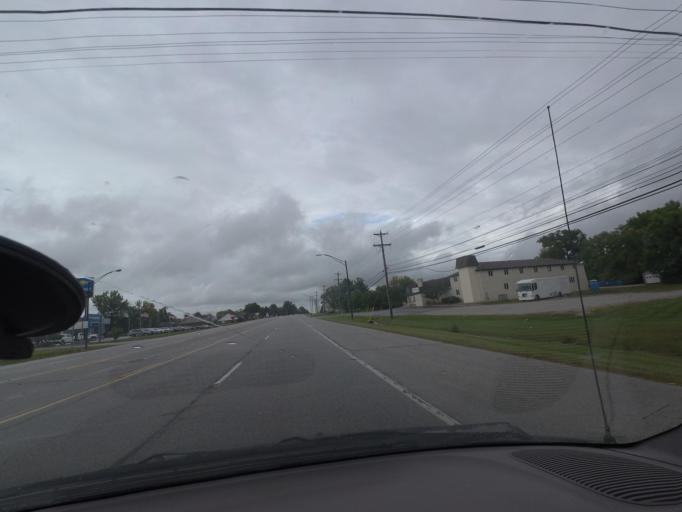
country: US
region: Indiana
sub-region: Montgomery County
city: Crawfordsville
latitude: 40.0645
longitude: -86.9081
